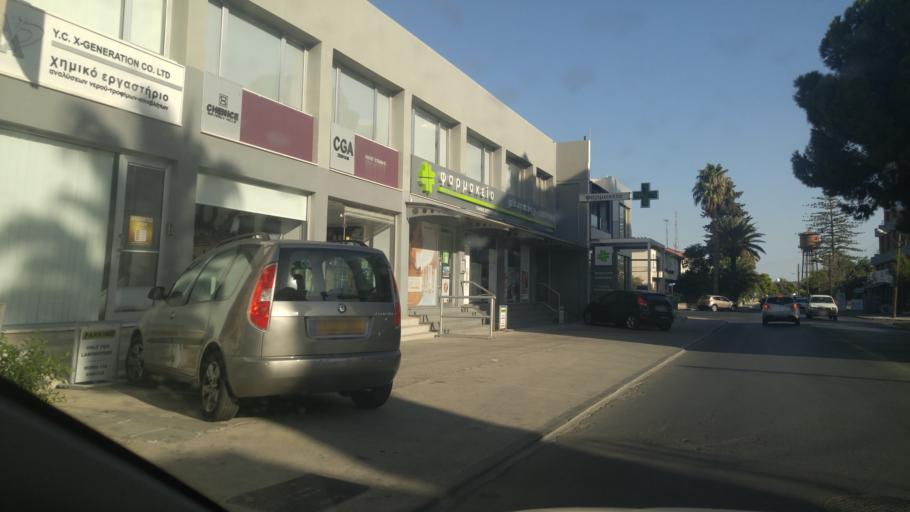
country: CY
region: Limassol
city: Limassol
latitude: 34.6806
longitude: 33.0348
